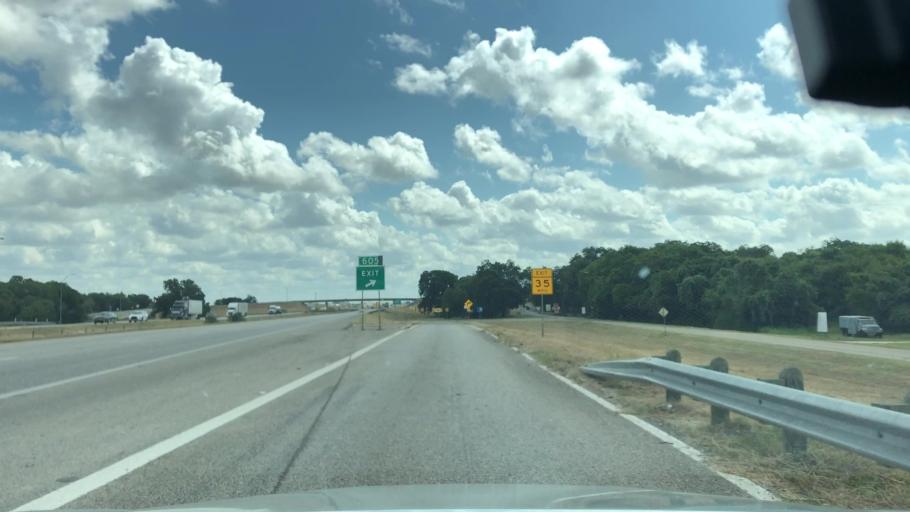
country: US
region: Texas
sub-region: Guadalupe County
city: McQueeney
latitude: 29.5685
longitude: -98.0200
